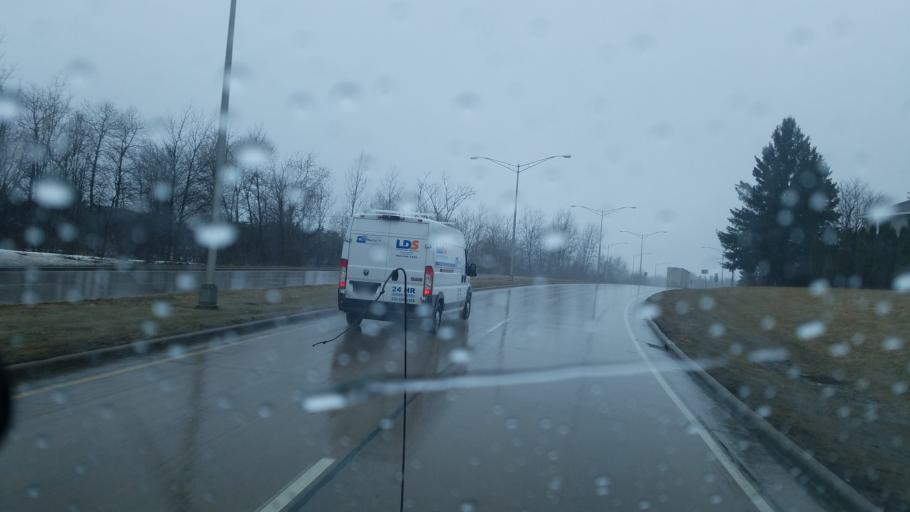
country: US
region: Wisconsin
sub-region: Wood County
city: Marshfield
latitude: 44.6723
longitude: -90.1850
